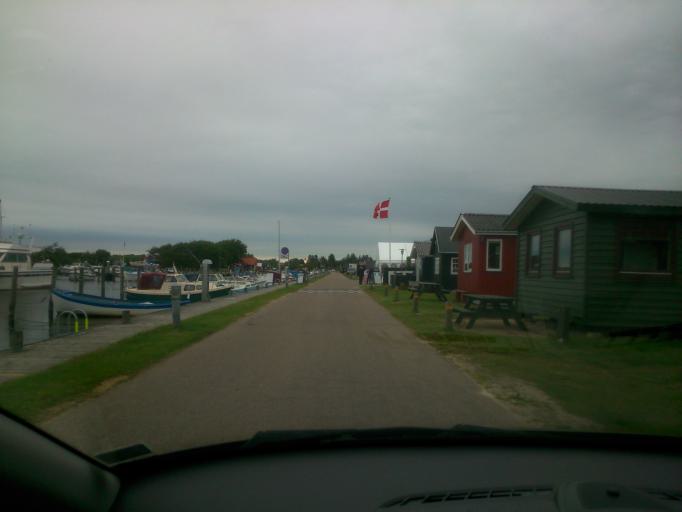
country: DK
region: Central Jutland
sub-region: Ringkobing-Skjern Kommune
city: Skjern
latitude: 55.9532
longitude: 8.3701
